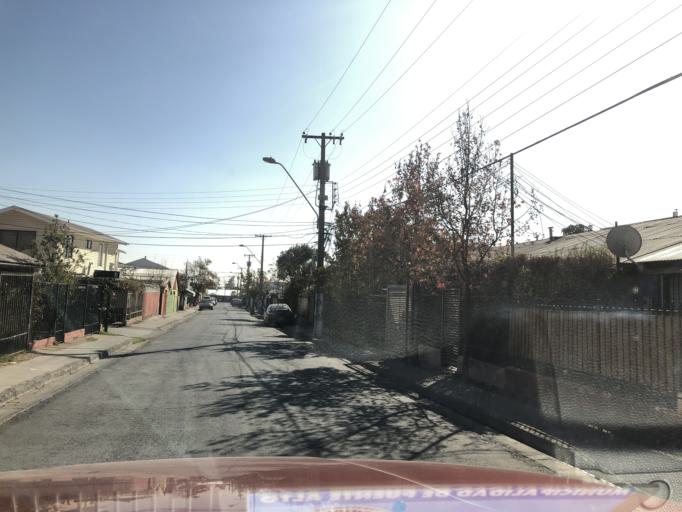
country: CL
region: Santiago Metropolitan
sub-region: Provincia de Cordillera
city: Puente Alto
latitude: -33.5749
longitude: -70.5737
